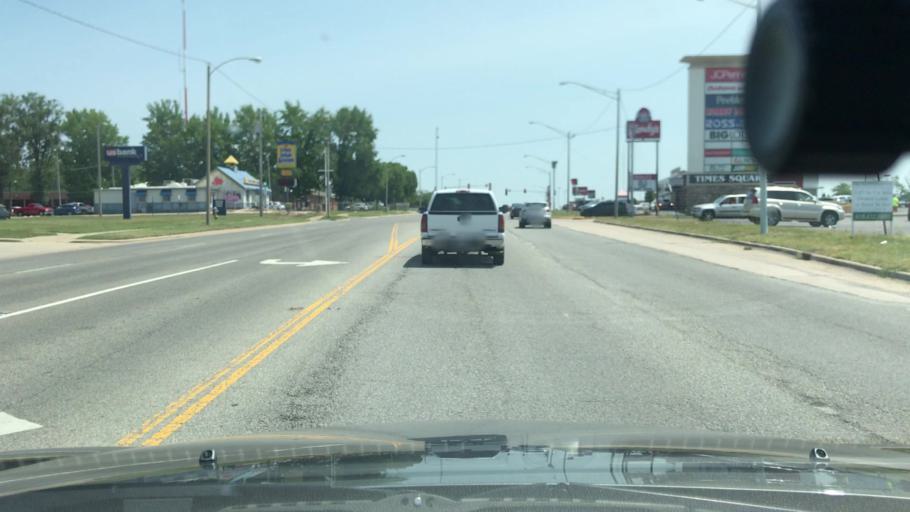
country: US
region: Illinois
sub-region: Jefferson County
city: Mount Vernon
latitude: 38.3142
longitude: -88.9415
